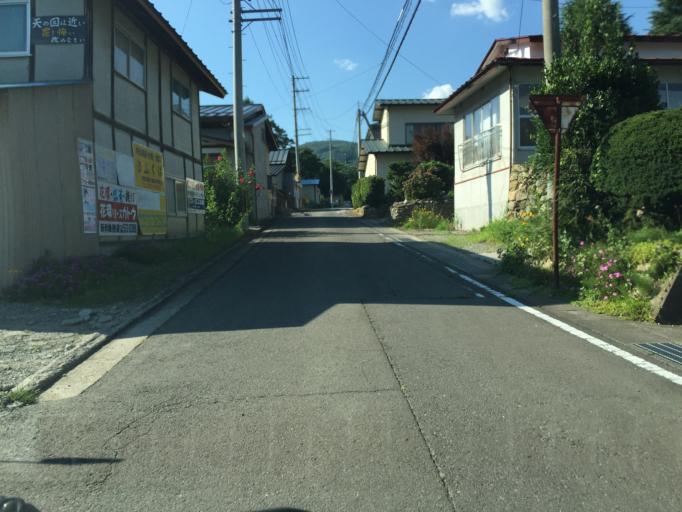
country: JP
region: Fukushima
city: Hobaramachi
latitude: 37.9193
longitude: 140.4245
